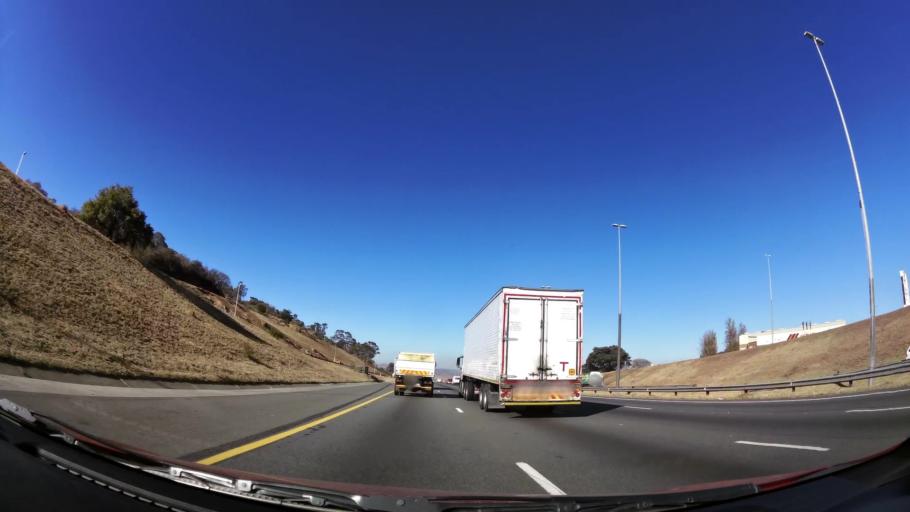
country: ZA
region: Gauteng
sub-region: City of Johannesburg Metropolitan Municipality
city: Soweto
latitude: -26.2779
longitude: 27.9473
